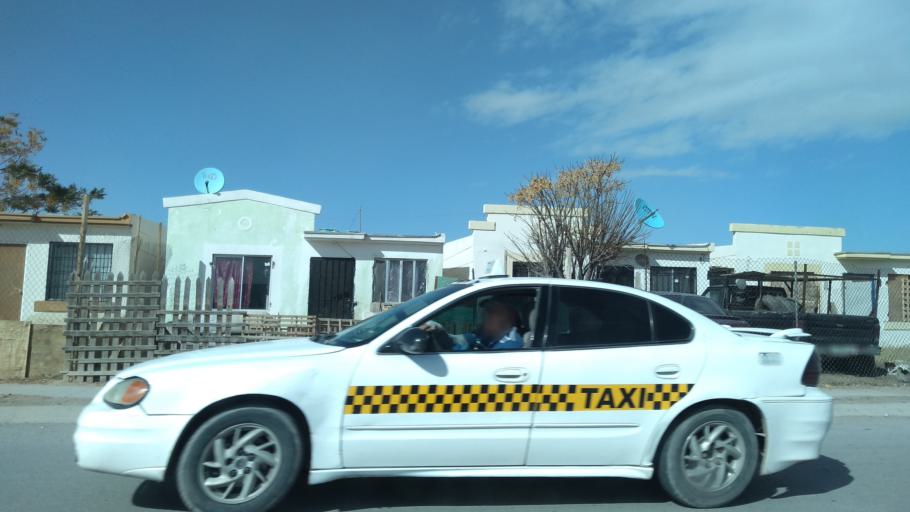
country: US
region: Texas
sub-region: El Paso County
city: San Elizario
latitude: 31.5641
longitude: -106.3356
